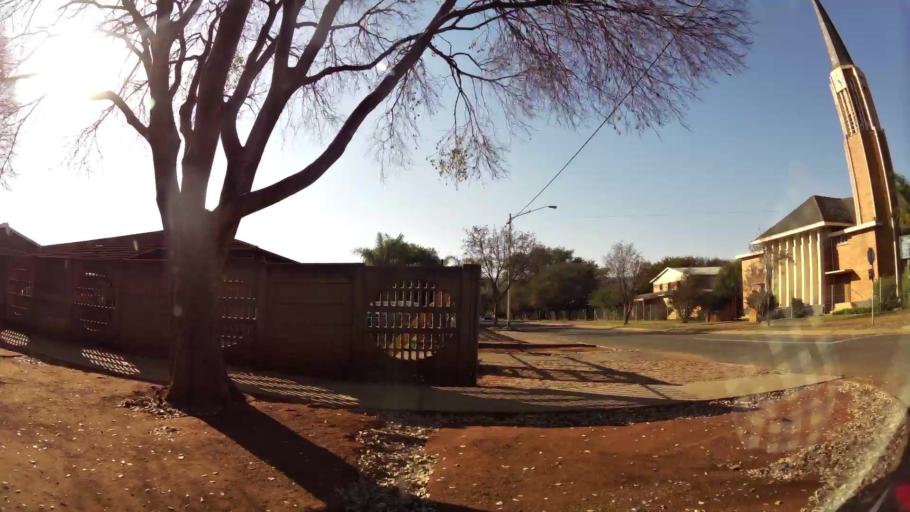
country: ZA
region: Gauteng
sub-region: City of Tshwane Metropolitan Municipality
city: Pretoria
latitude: -25.7138
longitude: 28.1499
